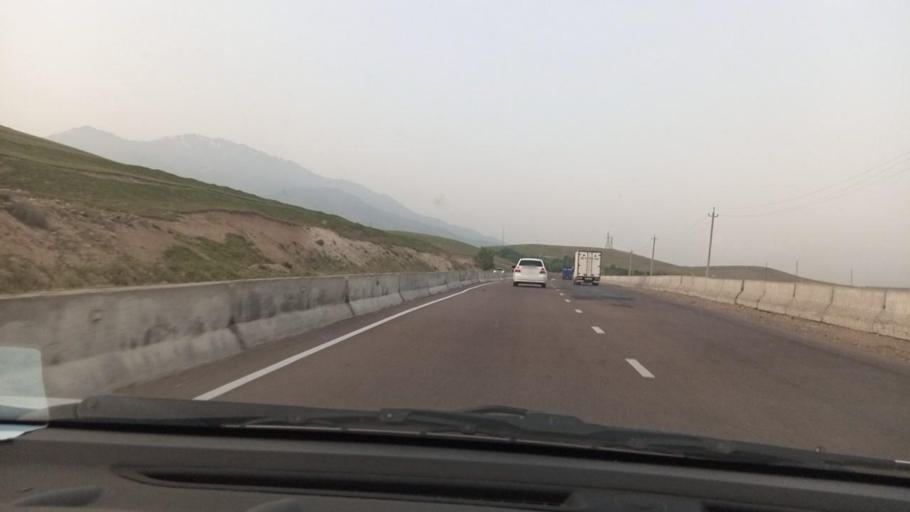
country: UZ
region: Toshkent
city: Angren
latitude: 41.0566
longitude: 70.1671
